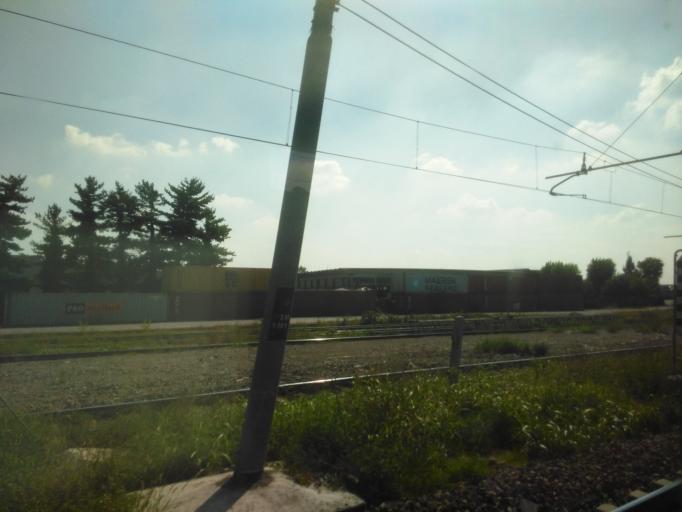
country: IT
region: Lombardy
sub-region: Citta metropolitana di Milano
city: San Bovio-San Felice
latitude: 45.4827
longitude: 9.3113
